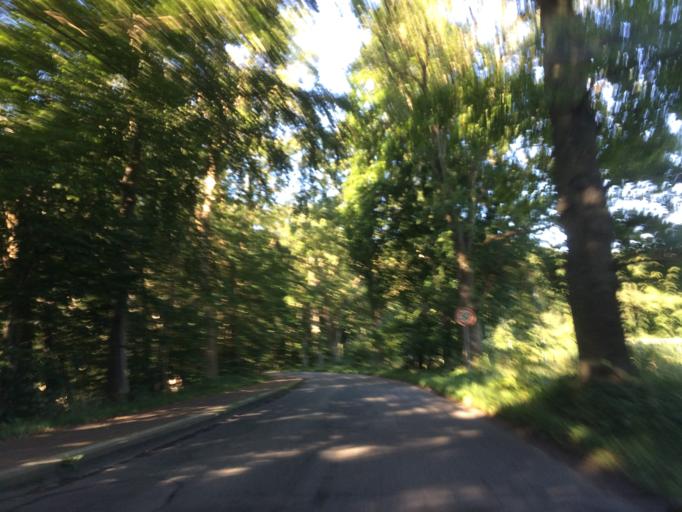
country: DE
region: Schleswig-Holstein
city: Bosdorf
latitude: 54.1564
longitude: 10.4731
